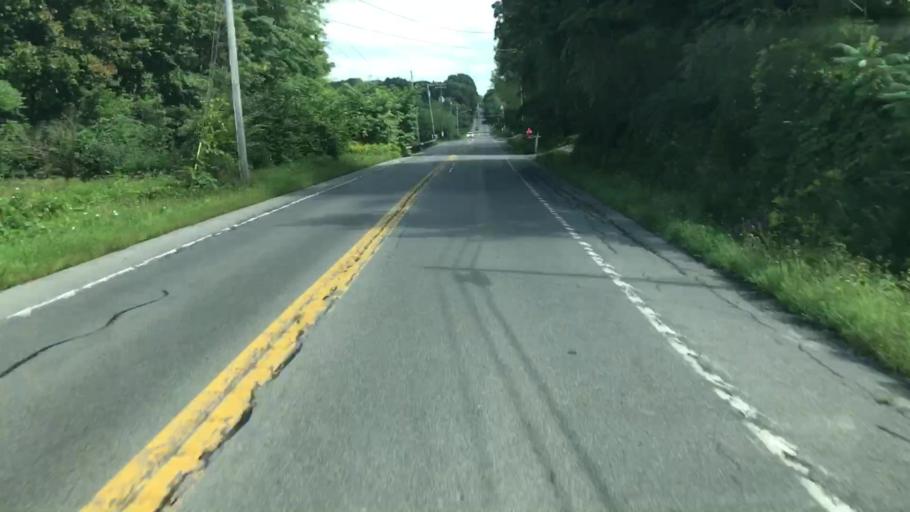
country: US
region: New York
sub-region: Onondaga County
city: Marcellus
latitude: 42.9843
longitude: -76.2970
